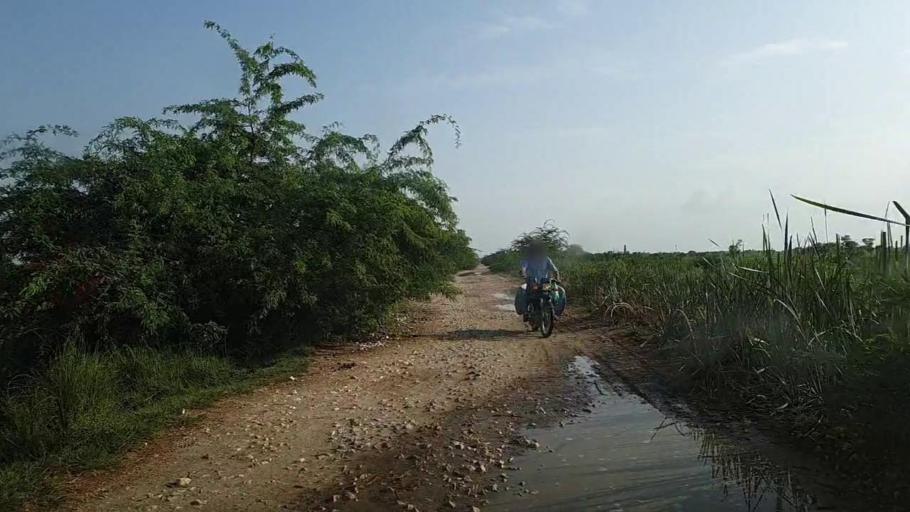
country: PK
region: Sindh
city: Pad Idan
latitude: 26.8150
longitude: 68.2371
